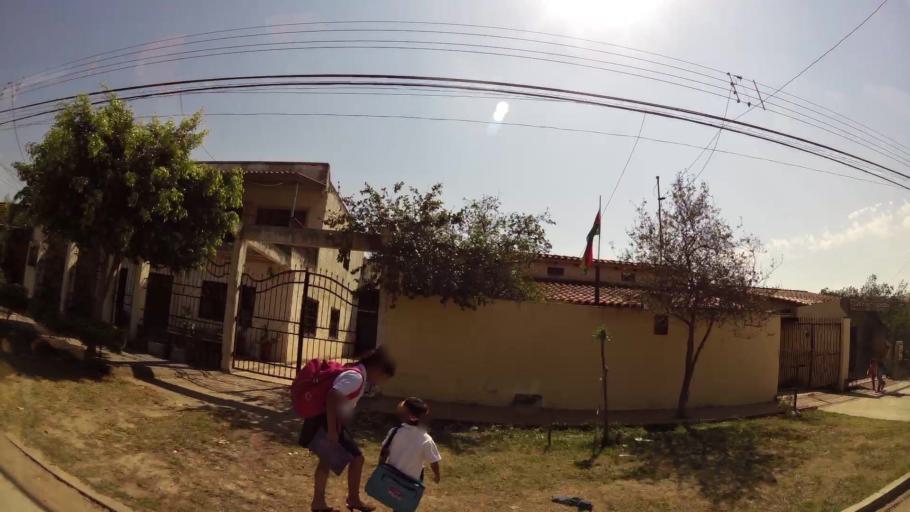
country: BO
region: Santa Cruz
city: Santa Cruz de la Sierra
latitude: -17.7471
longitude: -63.1460
